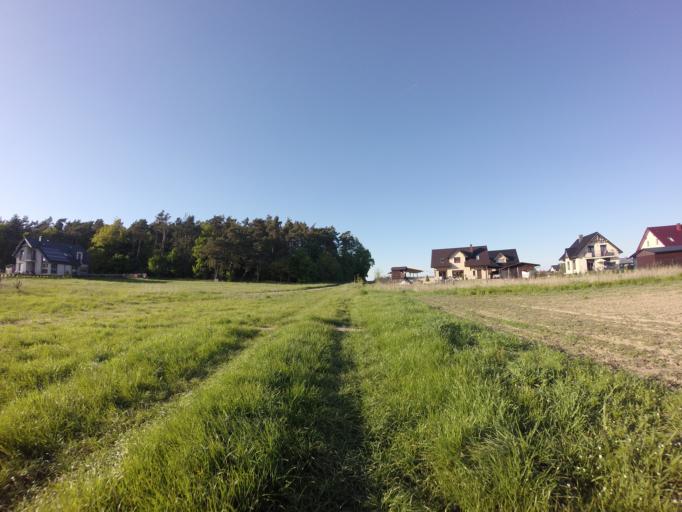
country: PL
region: West Pomeranian Voivodeship
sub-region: Powiat choszczenski
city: Choszczno
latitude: 53.1580
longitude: 15.3838
